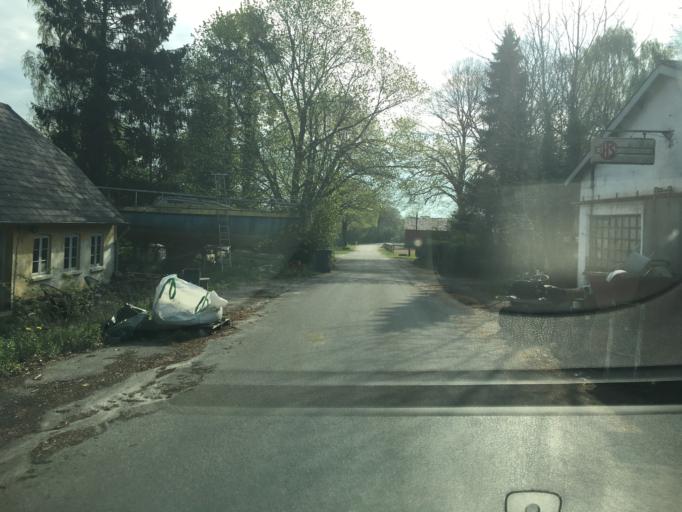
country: DK
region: South Denmark
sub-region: Haderslev Kommune
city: Vojens
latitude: 55.1875
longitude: 9.3864
